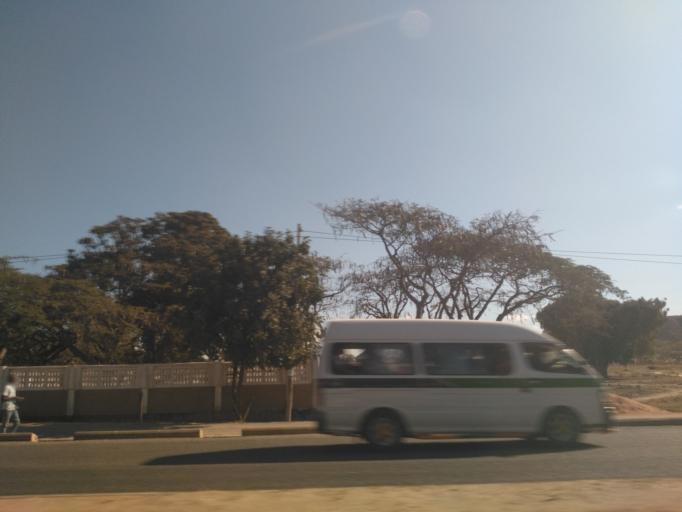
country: TZ
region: Dodoma
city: Dodoma
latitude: -6.1748
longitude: 35.7375
